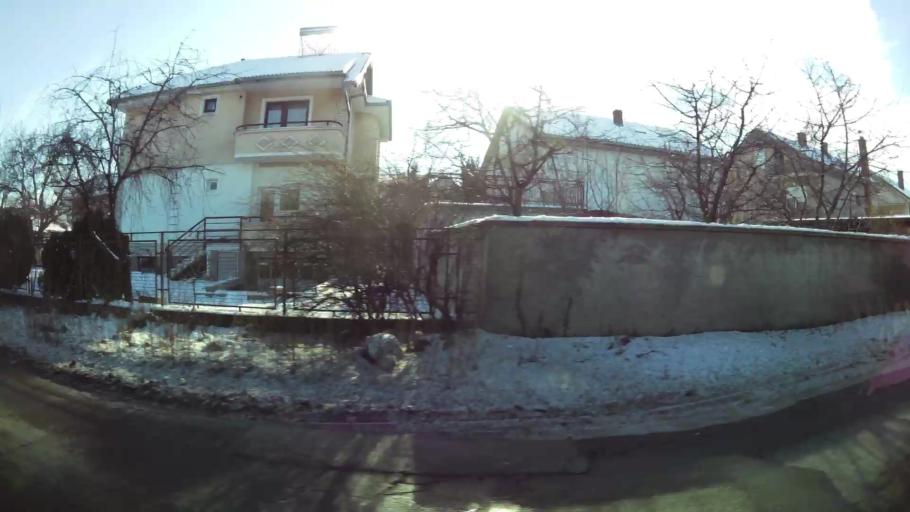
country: MK
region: Saraj
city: Saraj
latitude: 42.0108
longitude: 21.3480
